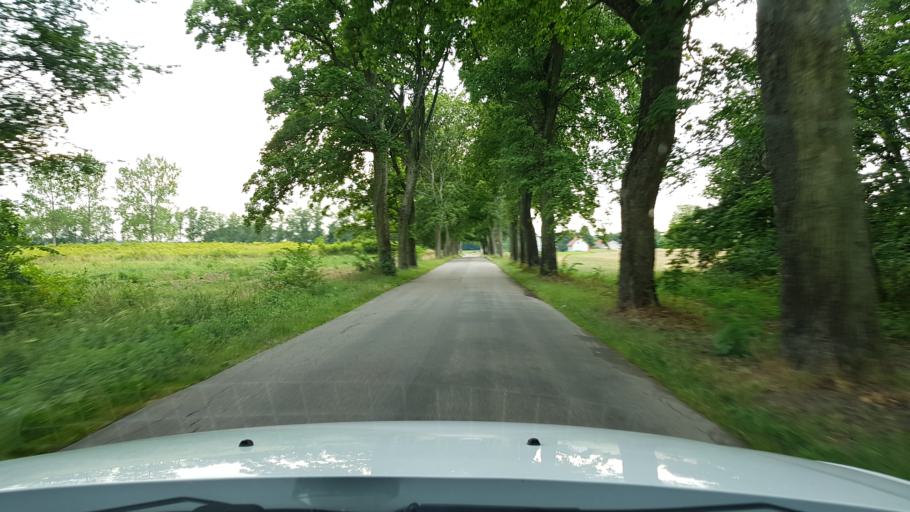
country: PL
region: West Pomeranian Voivodeship
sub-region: Powiat drawski
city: Wierzchowo
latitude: 53.4758
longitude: 16.0633
